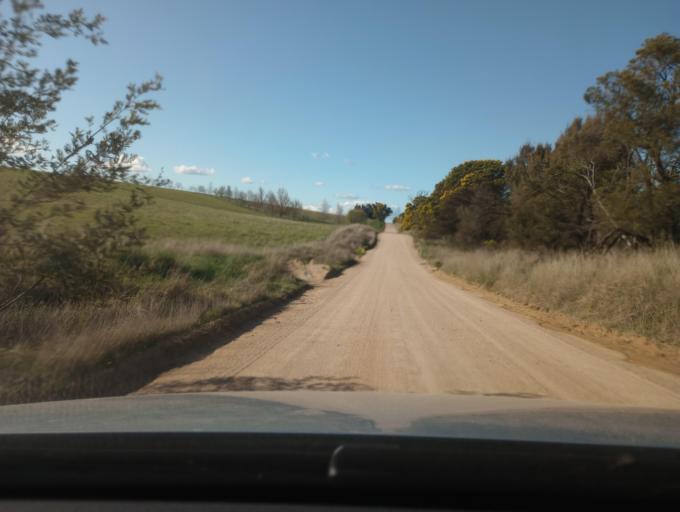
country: AU
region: New South Wales
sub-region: Blayney
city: Millthorpe
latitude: -33.4074
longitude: 149.3070
